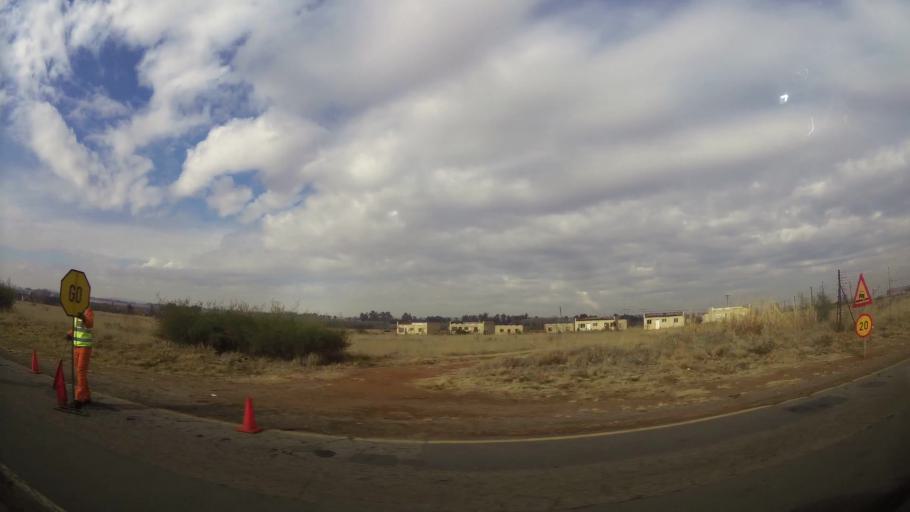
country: ZA
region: Gauteng
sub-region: Sedibeng District Municipality
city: Meyerton
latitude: -26.5584
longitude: 28.0547
